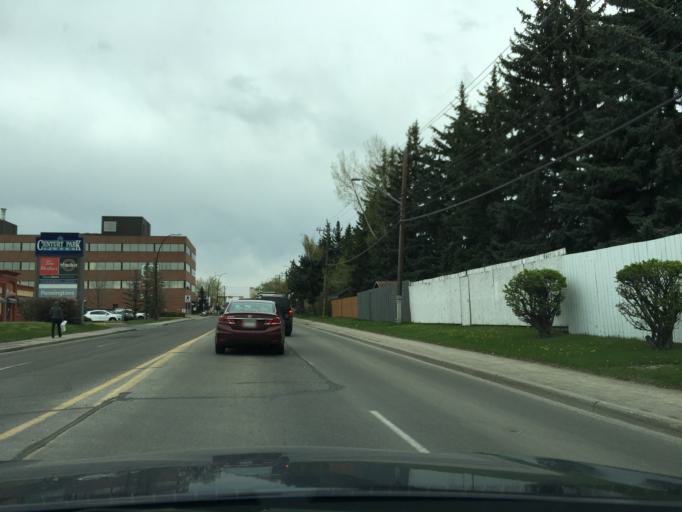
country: CA
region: Alberta
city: Calgary
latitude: 50.9591
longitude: -114.0688
